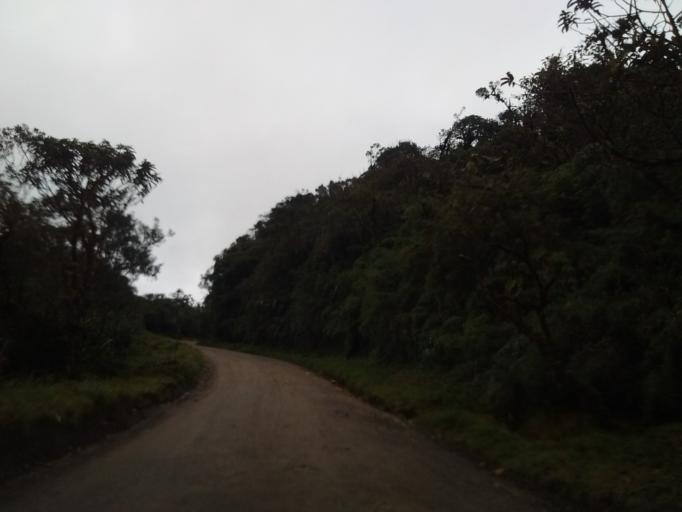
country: CO
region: Huila
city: Isnos
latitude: 2.1361
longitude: -76.3842
